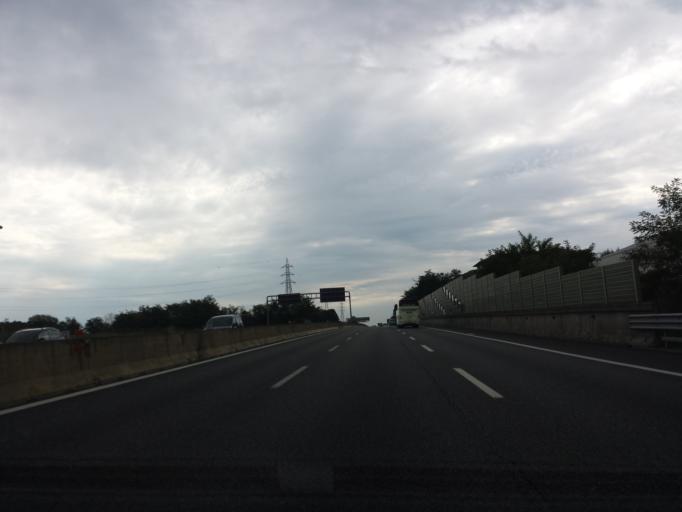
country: IT
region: Lombardy
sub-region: Citta metropolitana di Milano
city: Rescaldina
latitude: 45.6075
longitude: 8.9344
